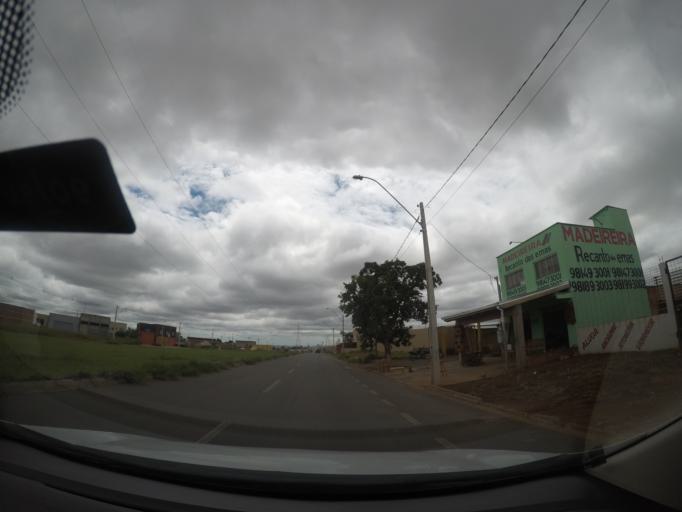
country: BR
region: Goias
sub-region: Goiania
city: Goiania
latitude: -16.7375
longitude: -49.3659
